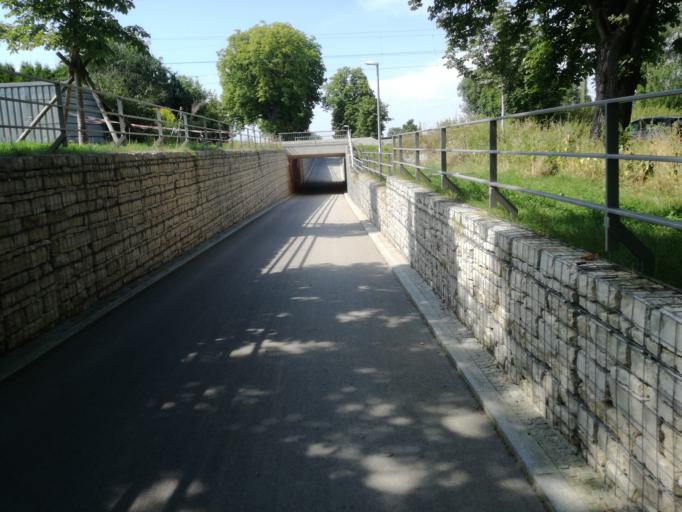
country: DE
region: Bavaria
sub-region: Upper Bavaria
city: Germering
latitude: 48.1379
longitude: 11.4015
